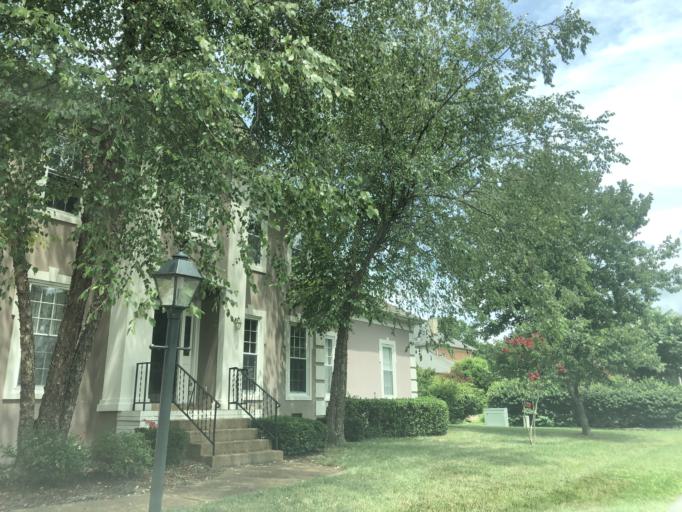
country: US
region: Tennessee
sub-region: Davidson County
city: Forest Hills
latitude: 36.0631
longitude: -86.8130
